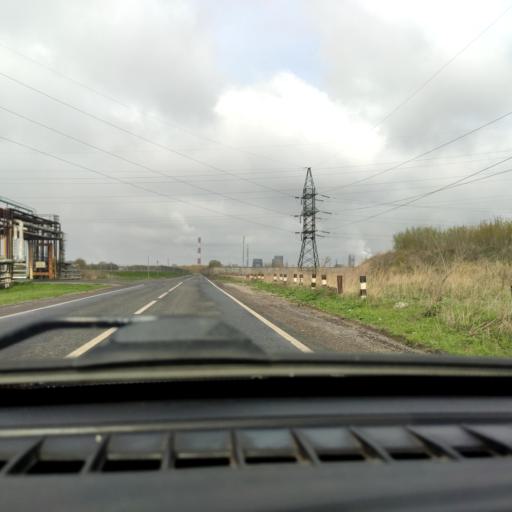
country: RU
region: Samara
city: Tol'yatti
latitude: 53.5406
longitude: 49.4863
